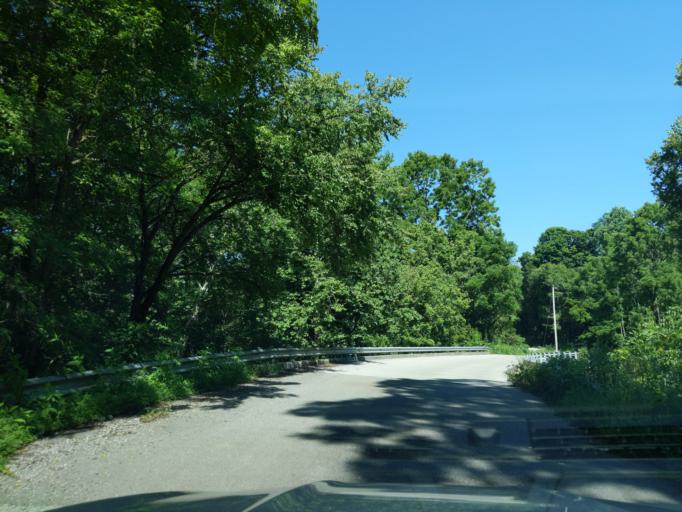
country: US
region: Indiana
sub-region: Ripley County
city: Osgood
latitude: 39.0749
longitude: -85.4252
